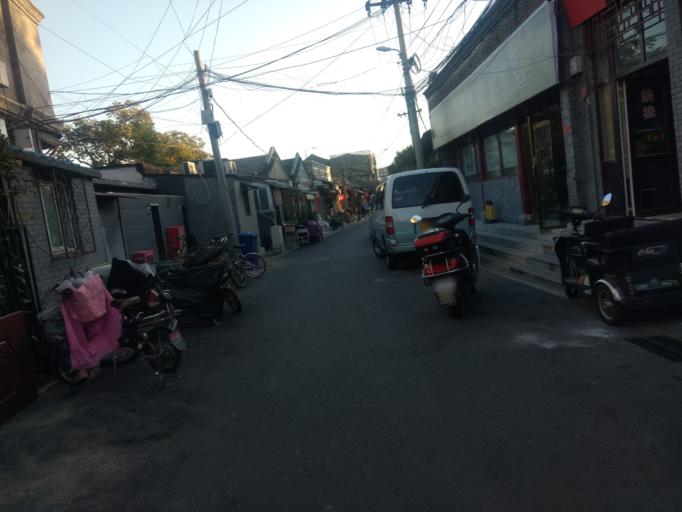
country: CN
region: Beijing
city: Beijing
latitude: 39.8899
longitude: 116.3791
